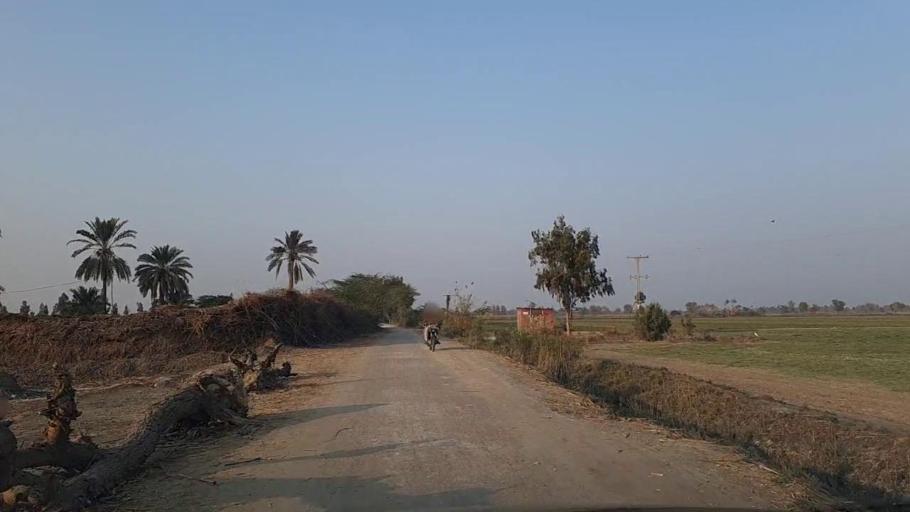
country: PK
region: Sindh
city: Daur
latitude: 26.4247
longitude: 68.3936
